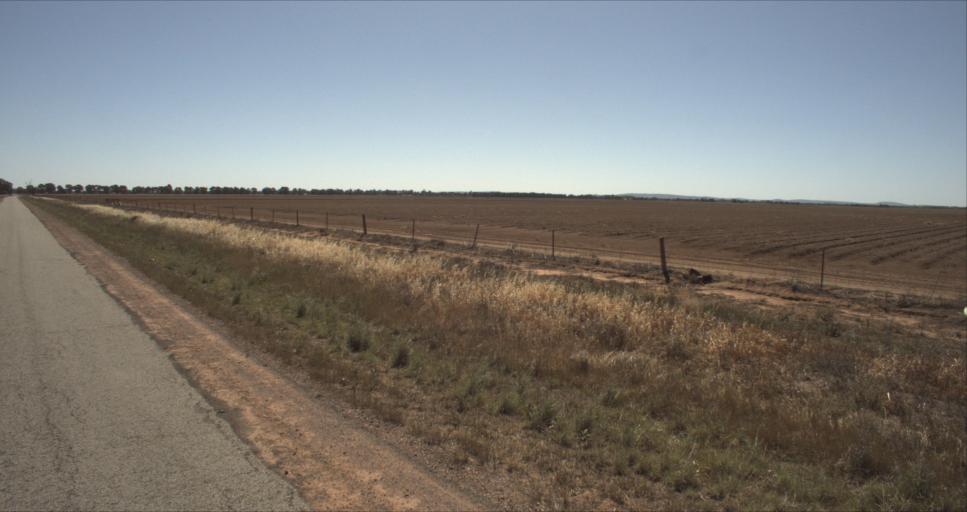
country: AU
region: New South Wales
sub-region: Leeton
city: Leeton
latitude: -34.5617
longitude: 146.3126
